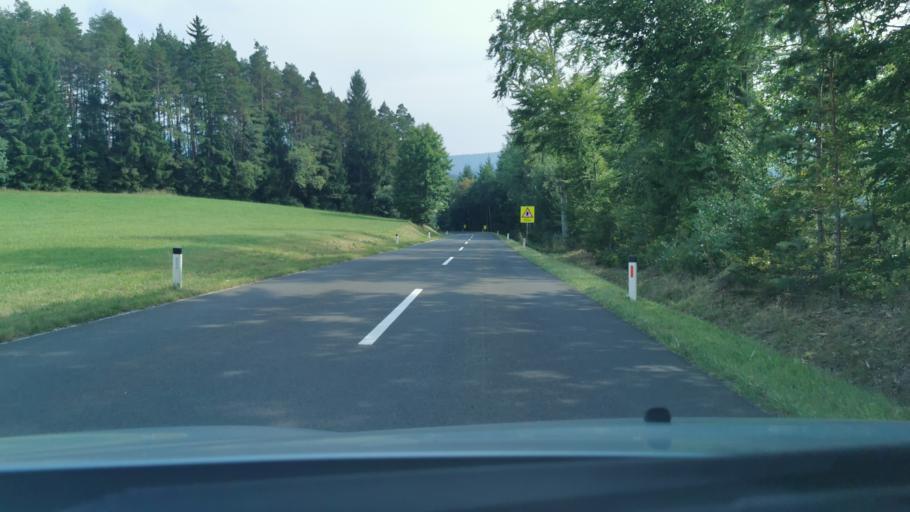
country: AT
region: Styria
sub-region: Politischer Bezirk Weiz
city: Birkfeld
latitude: 47.3923
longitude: 15.6694
